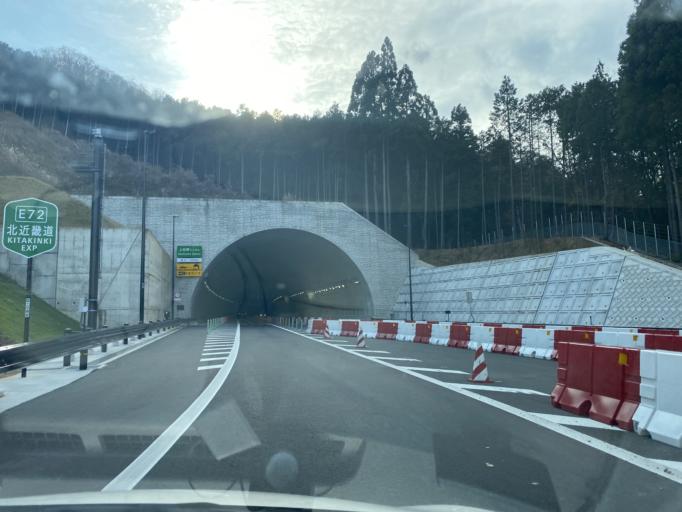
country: JP
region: Hyogo
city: Toyooka
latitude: 35.5066
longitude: 134.8017
